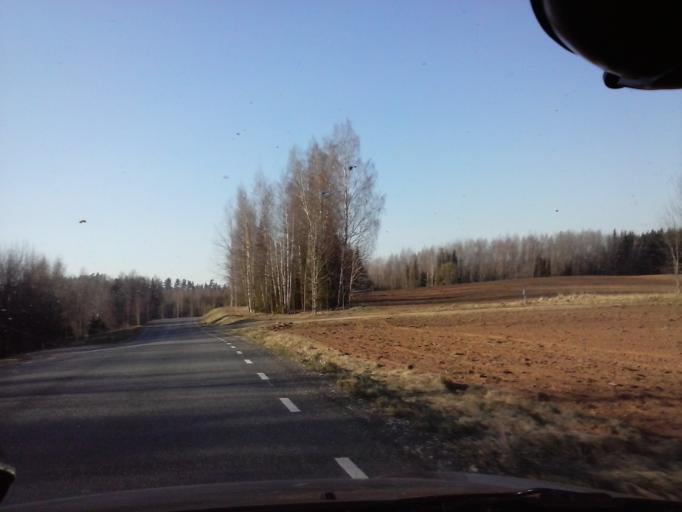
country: EE
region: Tartu
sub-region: UElenurme vald
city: Ulenurme
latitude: 58.1612
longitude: 26.8491
